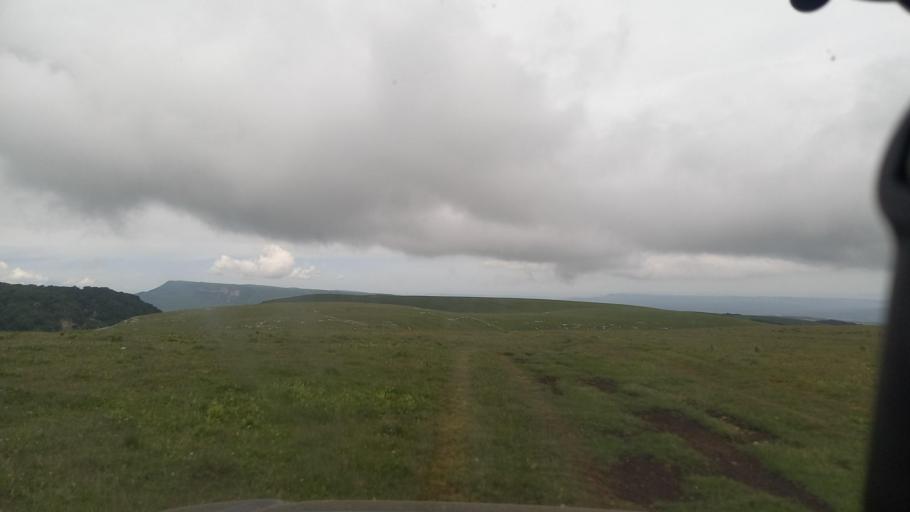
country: RU
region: Karachayevo-Cherkesiya
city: Pregradnaya
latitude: 43.9833
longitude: 41.2921
